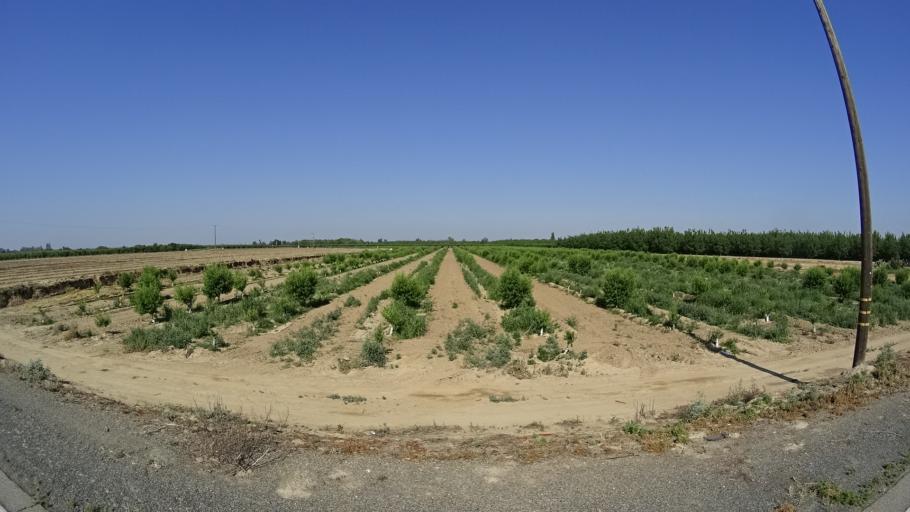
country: US
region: California
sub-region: Fresno County
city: Kingsburg
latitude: 36.4682
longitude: -119.5642
